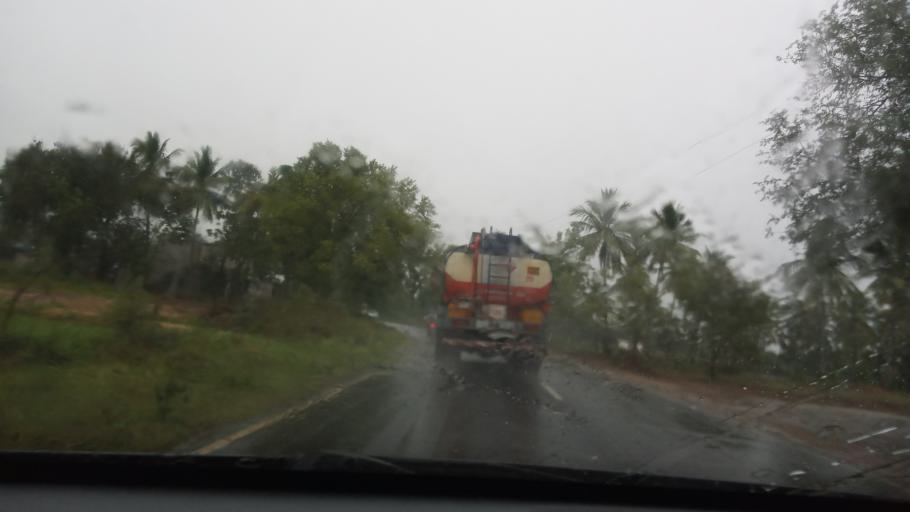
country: IN
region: Tamil Nadu
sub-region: Vellore
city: Kalavai
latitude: 12.8196
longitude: 79.4107
